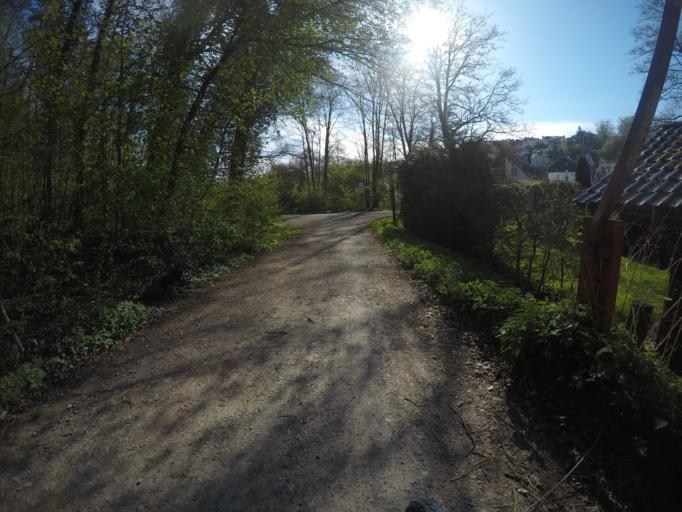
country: DE
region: Baden-Wuerttemberg
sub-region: Regierungsbezirk Stuttgart
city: Schlaitdorf
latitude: 48.6203
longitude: 9.2095
